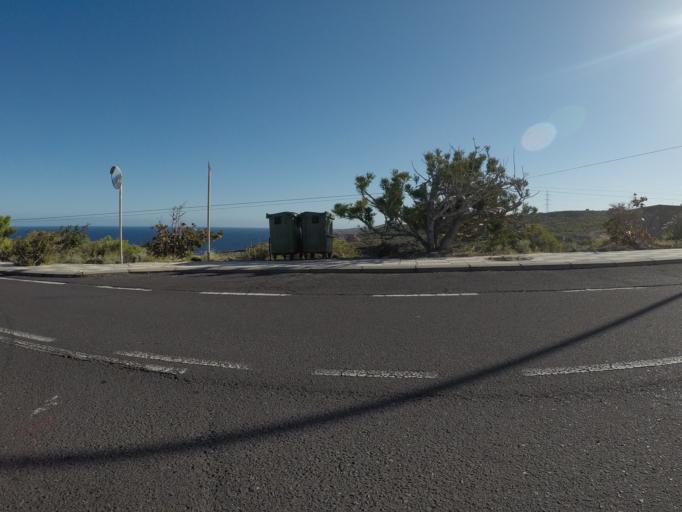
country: ES
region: Canary Islands
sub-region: Provincia de Santa Cruz de Tenerife
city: Fasnia
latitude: 28.2226
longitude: -16.4180
